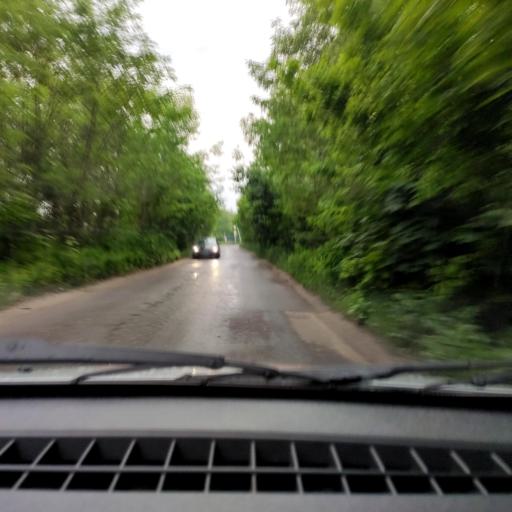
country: RU
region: Voronezj
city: Ramon'
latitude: 51.8484
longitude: 39.2352
